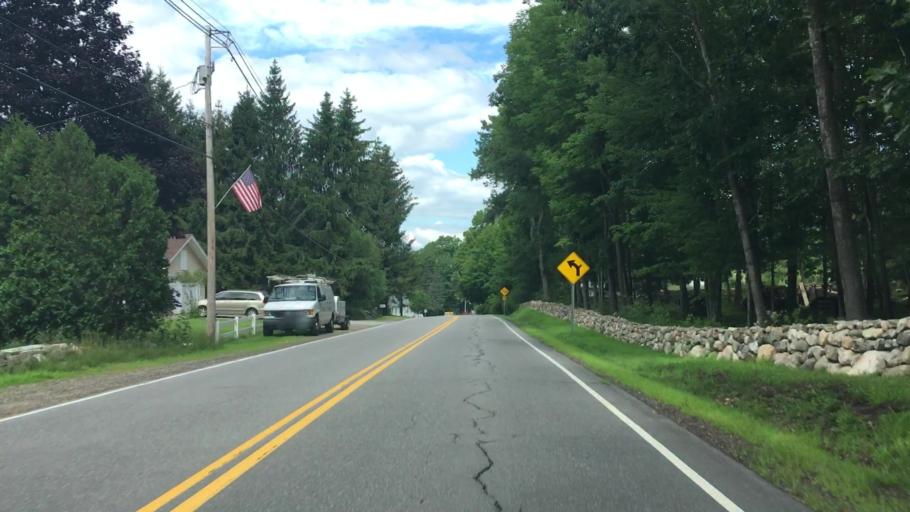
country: US
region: New Hampshire
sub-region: Belknap County
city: Meredith
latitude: 43.6131
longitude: -71.5277
